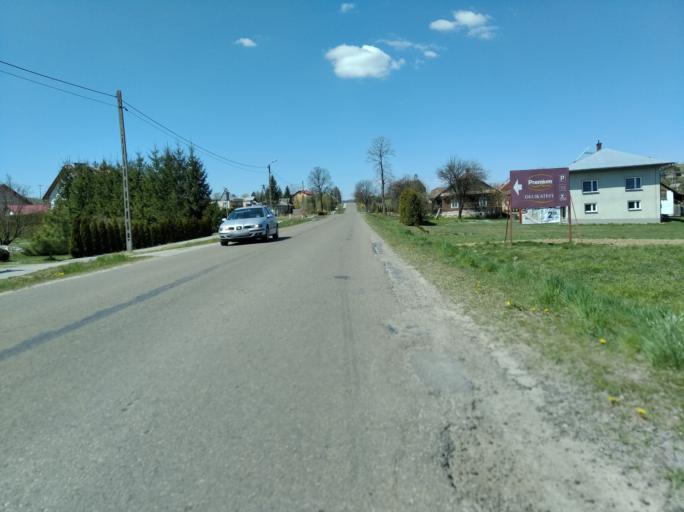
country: PL
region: Subcarpathian Voivodeship
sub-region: Powiat brzozowski
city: Dydnia
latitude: 49.6891
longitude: 22.1640
